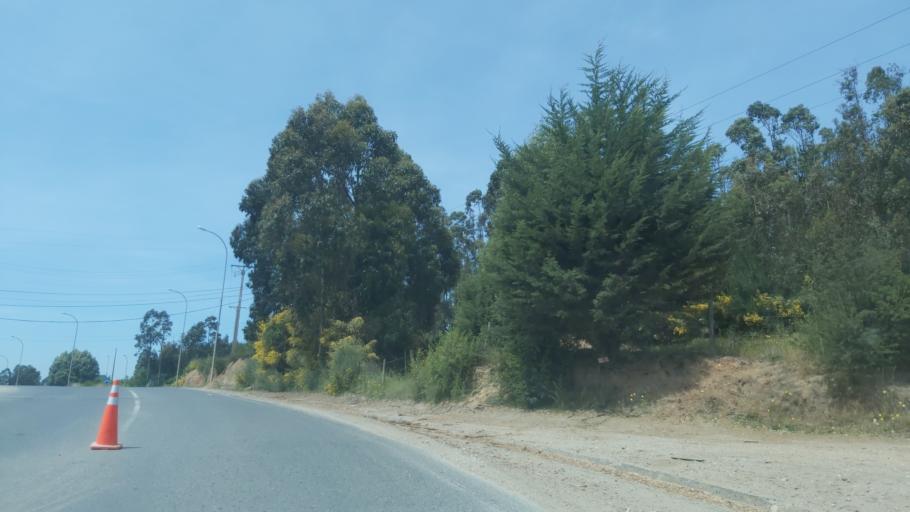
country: CL
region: Maule
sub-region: Provincia de Talca
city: Constitucion
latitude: -35.3675
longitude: -72.4030
